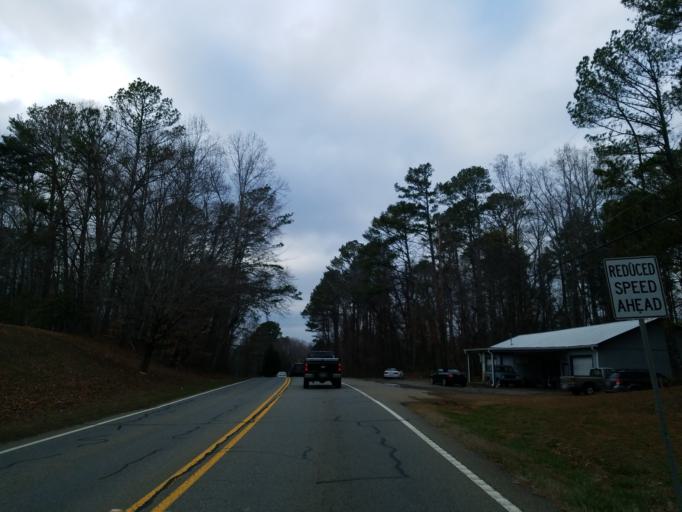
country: US
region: Georgia
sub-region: Cherokee County
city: Canton
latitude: 34.3107
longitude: -84.5344
